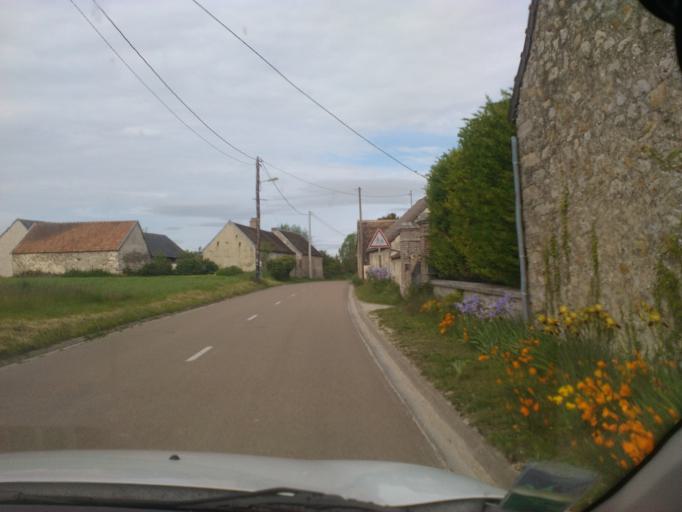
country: FR
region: Champagne-Ardenne
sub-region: Departement de l'Aube
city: Marigny-le-Chatel
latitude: 48.3509
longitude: 3.6545
